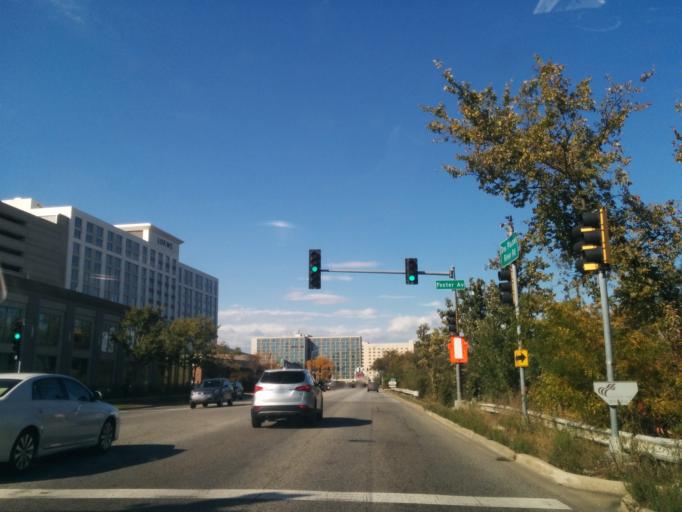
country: US
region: Illinois
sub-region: Cook County
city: Schiller Park
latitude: 41.9732
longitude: -87.8622
